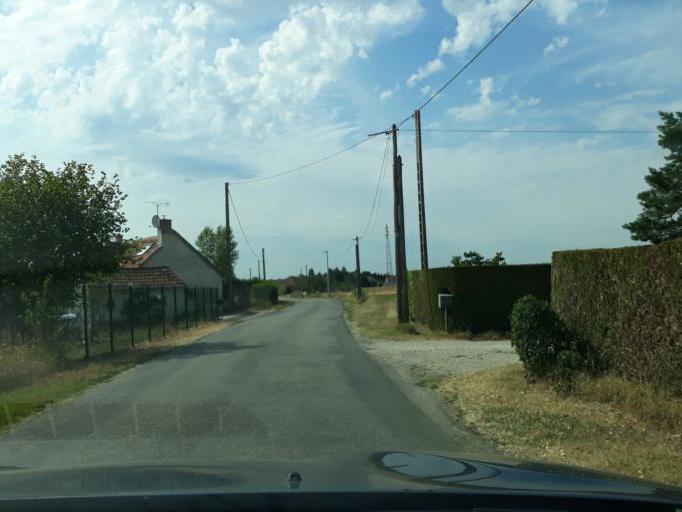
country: FR
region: Centre
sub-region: Departement du Loiret
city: Chateauneuf-sur-Loire
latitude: 47.8420
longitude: 2.1788
